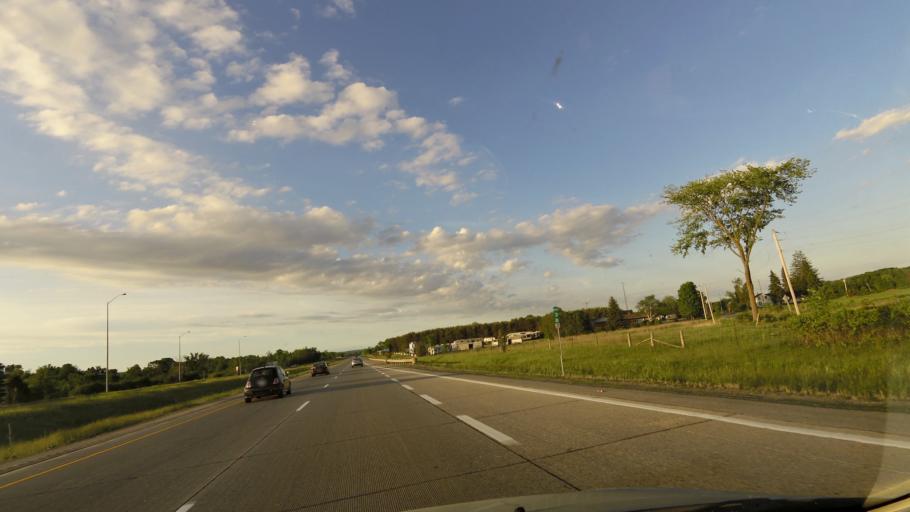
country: CA
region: Ontario
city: Omemee
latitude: 44.1873
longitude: -78.4612
